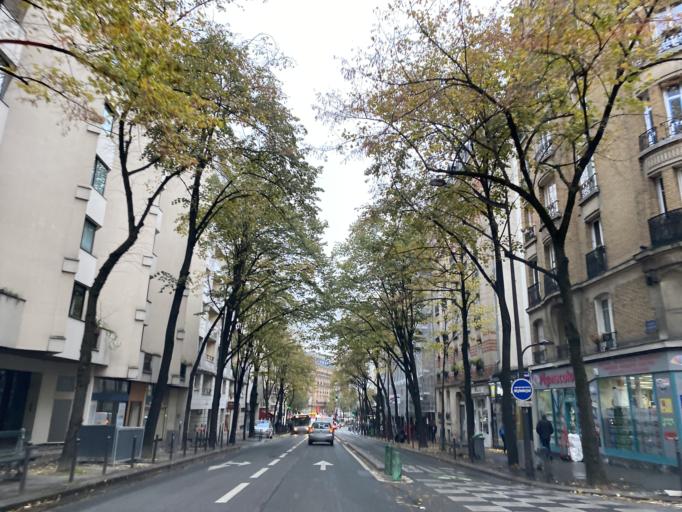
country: FR
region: Ile-de-France
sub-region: Departement de Seine-Saint-Denis
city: Le Pre-Saint-Gervais
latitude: 48.8731
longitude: 2.4048
